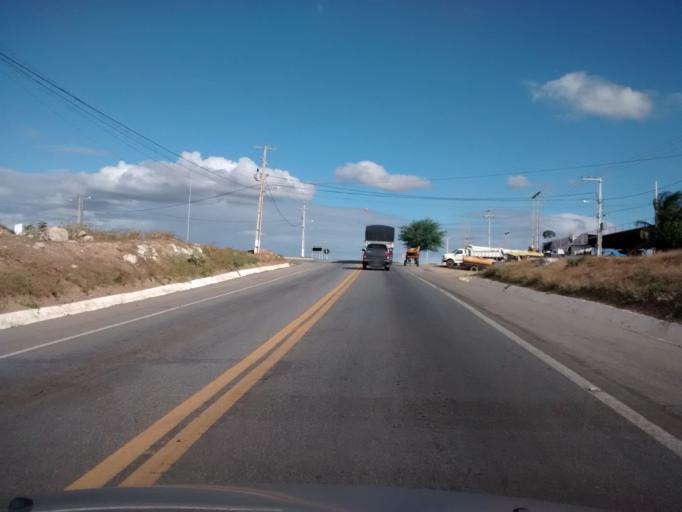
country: BR
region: Rio Grande do Norte
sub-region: Currais Novos
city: Currais Novos
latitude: -6.2734
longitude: -36.5239
